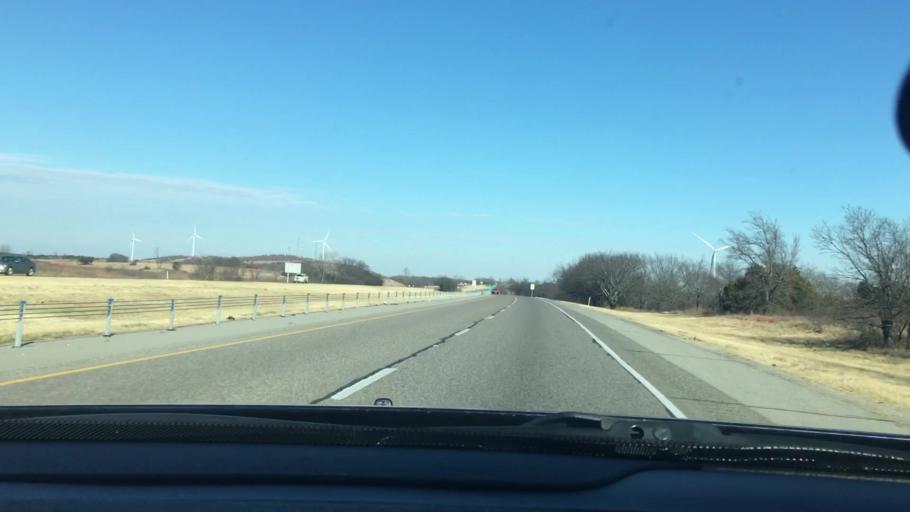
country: US
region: Oklahoma
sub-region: Murray County
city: Davis
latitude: 34.3866
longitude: -97.1416
